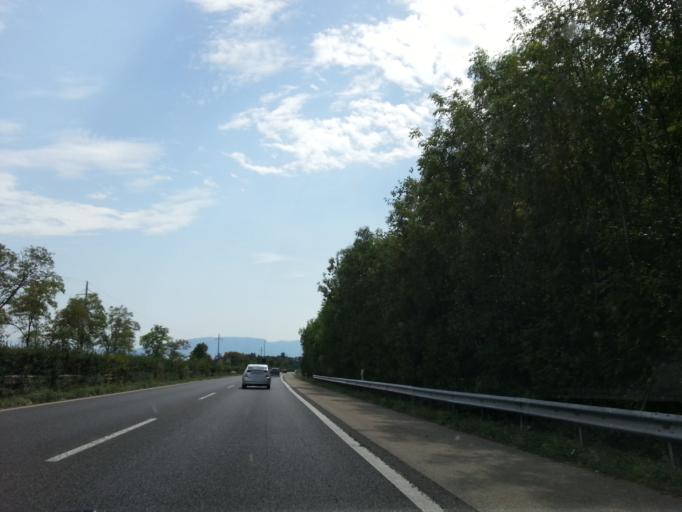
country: CH
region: Geneva
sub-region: Geneva
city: Versoix
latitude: 46.2960
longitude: 6.1459
